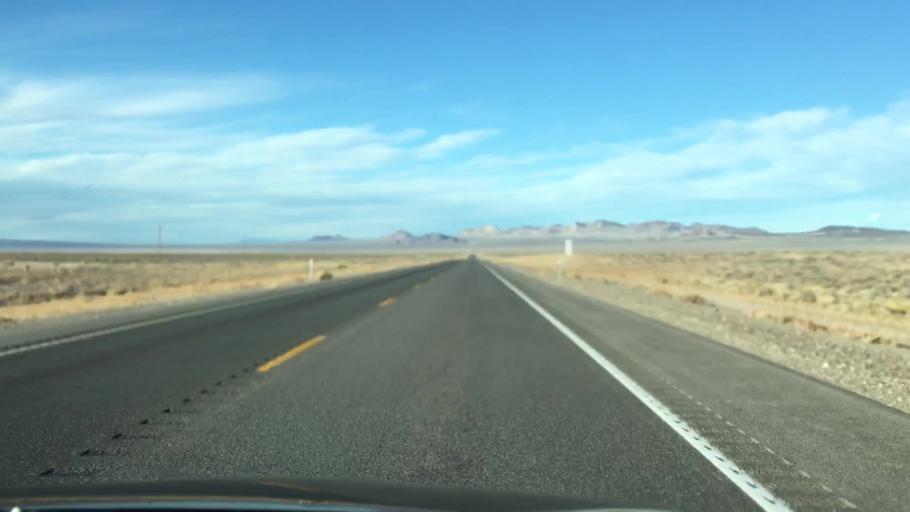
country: US
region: Nevada
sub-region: Esmeralda County
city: Goldfield
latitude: 37.8048
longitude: -117.2395
